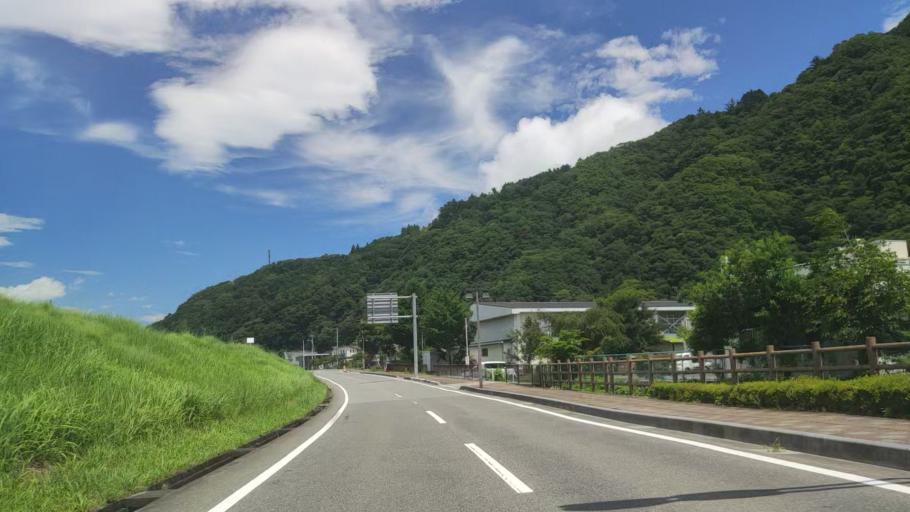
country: JP
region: Shizuoka
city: Fujinomiya
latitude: 35.3673
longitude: 138.4539
